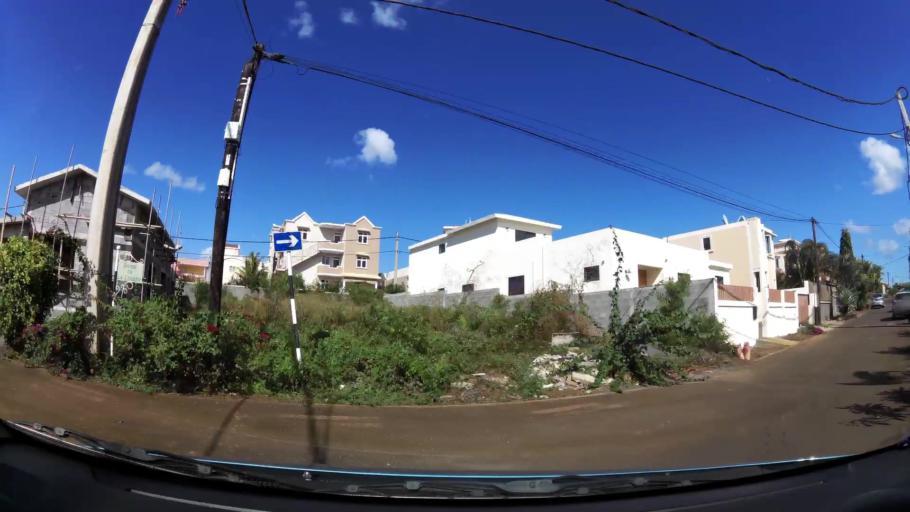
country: MU
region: Black River
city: Albion
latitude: -20.2223
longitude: 57.4148
